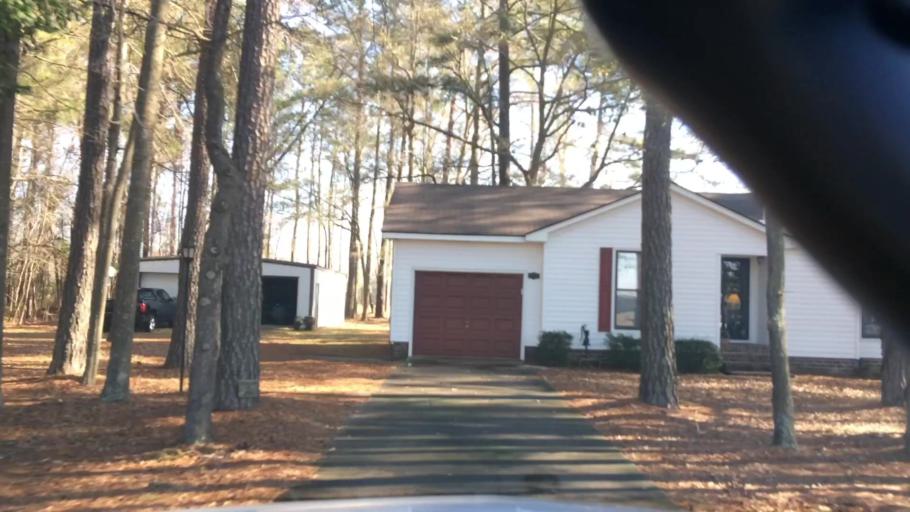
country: US
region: North Carolina
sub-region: Pitt County
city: Grifton
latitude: 35.4133
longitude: -77.4345
